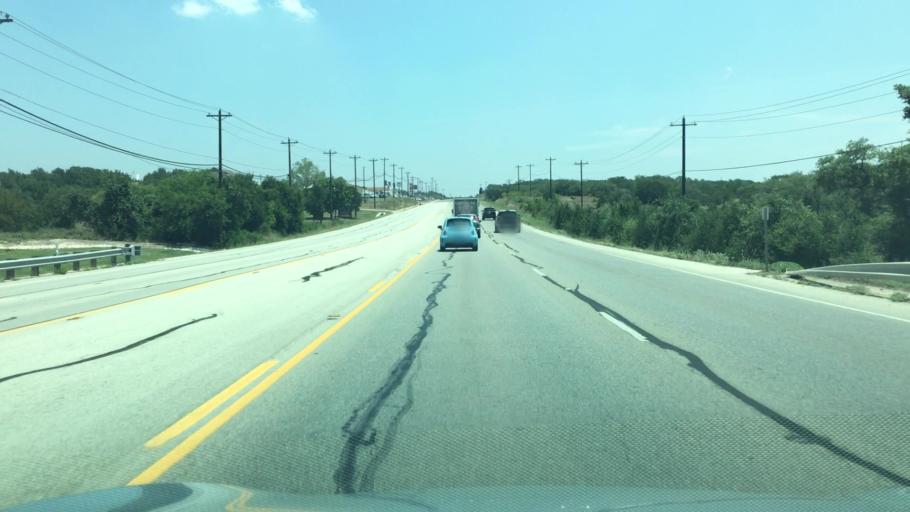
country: US
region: Texas
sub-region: Travis County
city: Bee Cave
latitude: 30.2264
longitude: -97.9457
